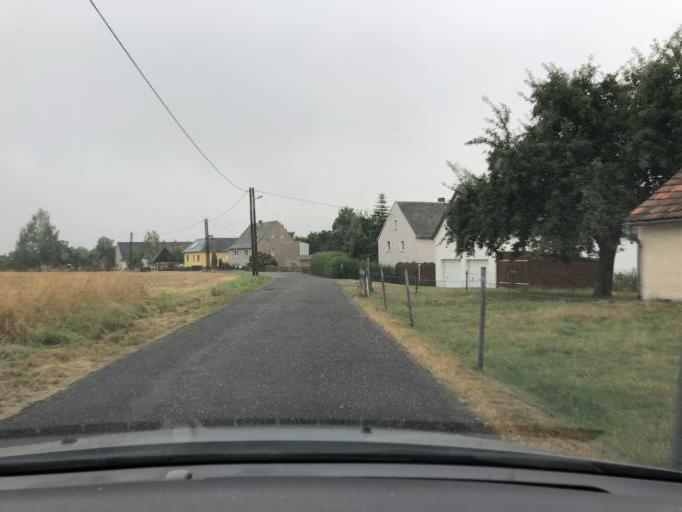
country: DE
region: Thuringia
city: Langenleuba-Niederhain
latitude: 50.9937
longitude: 12.6485
